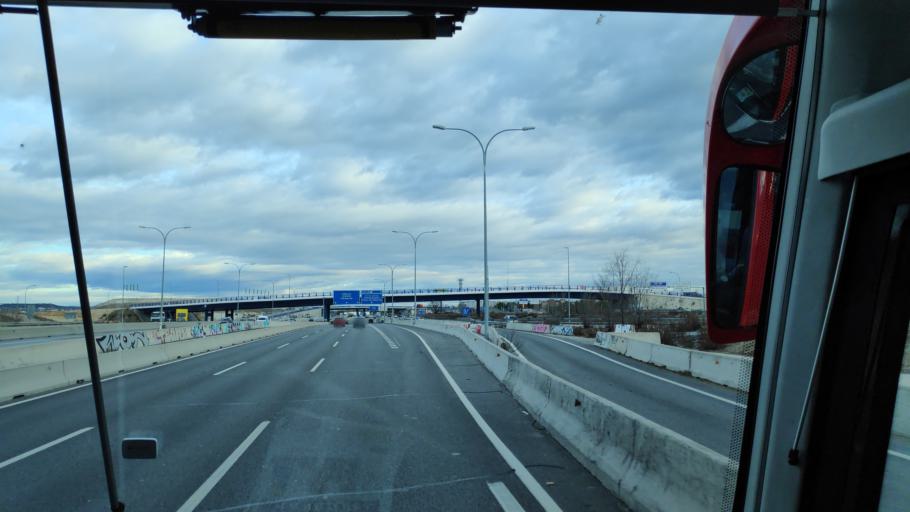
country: ES
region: Madrid
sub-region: Provincia de Madrid
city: Villa de Vallecas
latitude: 40.3708
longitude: -3.5917
